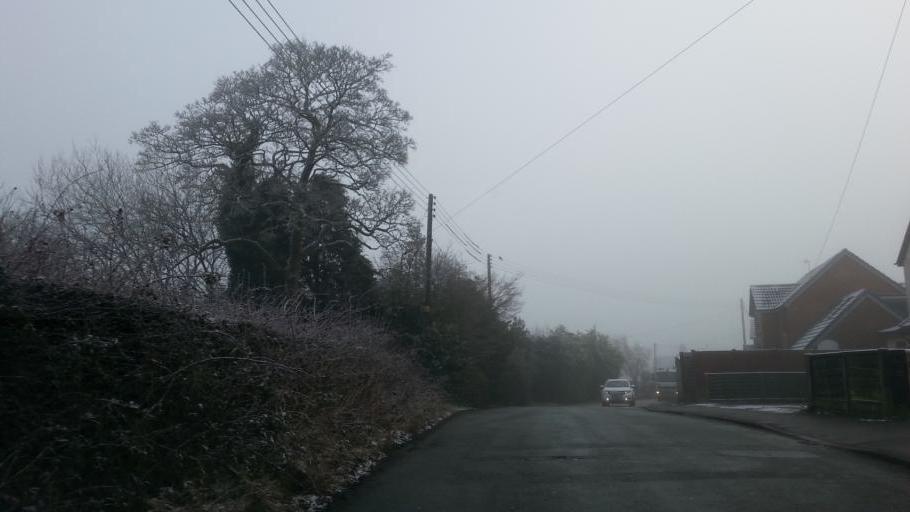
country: GB
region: England
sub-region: Staffordshire
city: Biddulph
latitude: 53.1254
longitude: -2.1801
